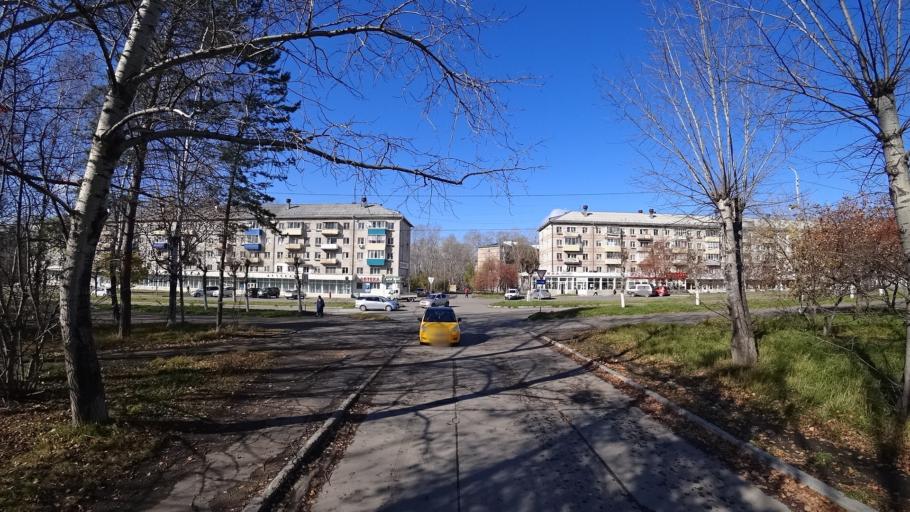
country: RU
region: Khabarovsk Krai
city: Amursk
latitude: 50.2253
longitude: 136.9087
